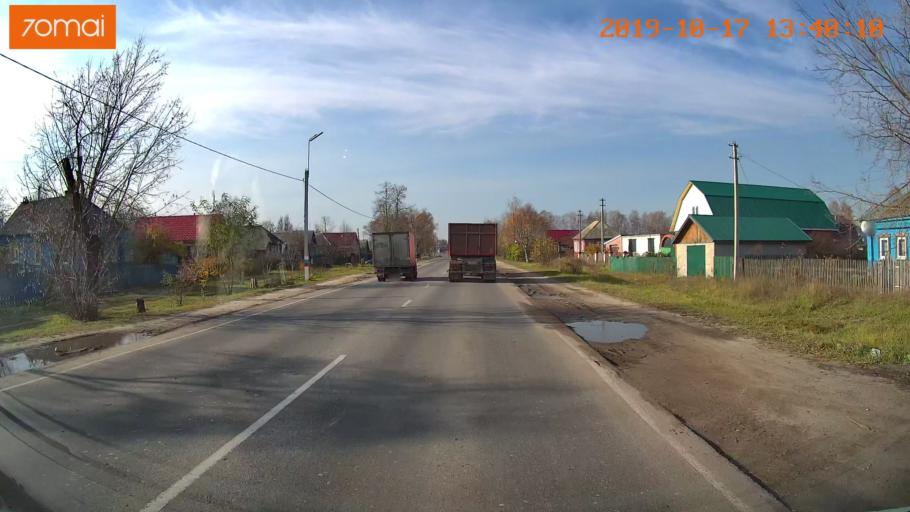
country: RU
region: Rjazan
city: Tuma
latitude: 55.1473
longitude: 40.5764
